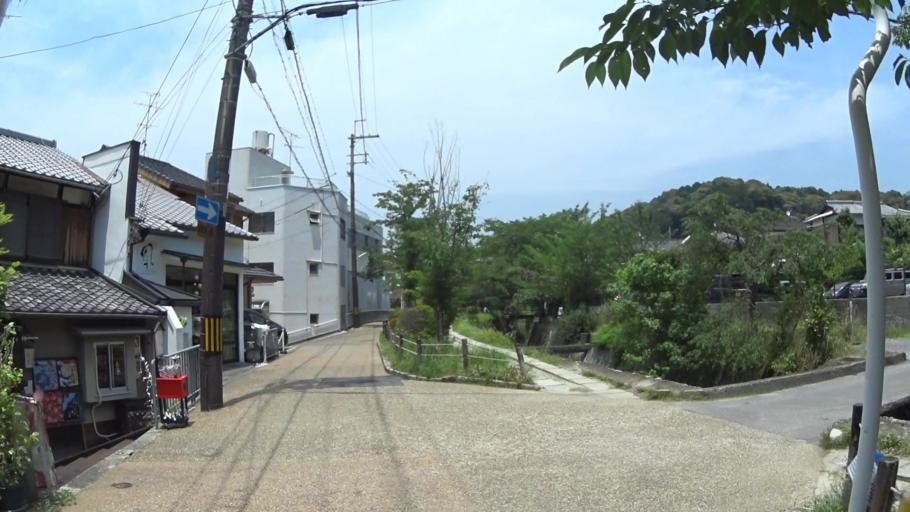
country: JP
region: Kyoto
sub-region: Kyoto-shi
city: Kamigyo-ku
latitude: 35.0258
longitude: 135.7956
